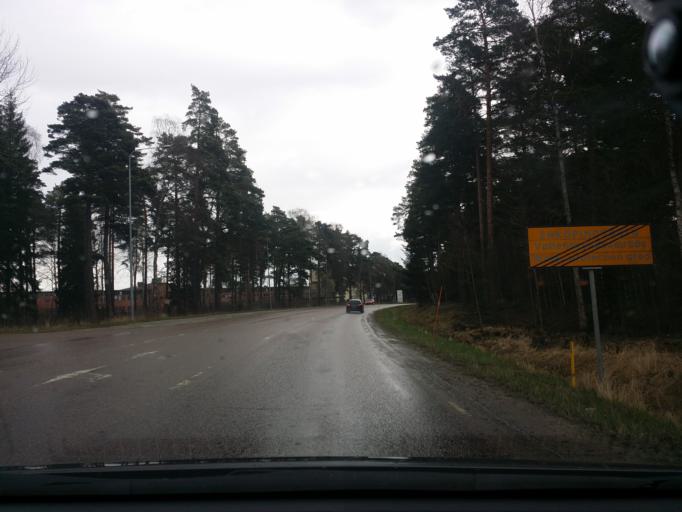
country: SE
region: Uppsala
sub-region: Enkopings Kommun
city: Enkoping
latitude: 59.6453
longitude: 17.1072
